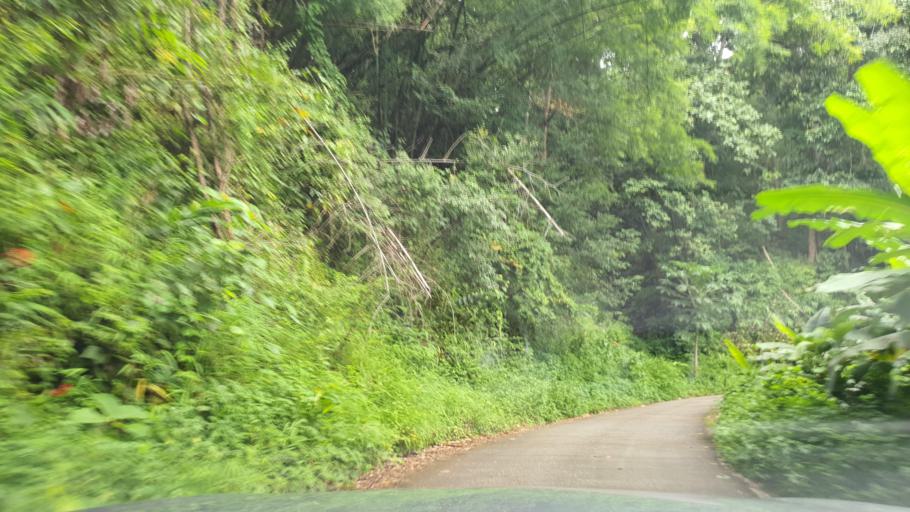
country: TH
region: Chiang Mai
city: Mae Taeng
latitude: 19.2333
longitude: 98.9280
